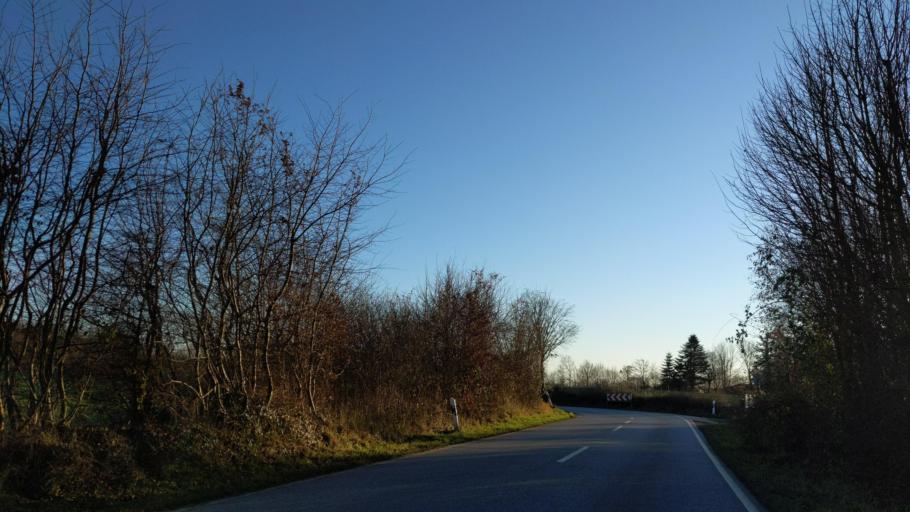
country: DE
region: Schleswig-Holstein
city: Travemuende
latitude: 53.9712
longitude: 10.8429
